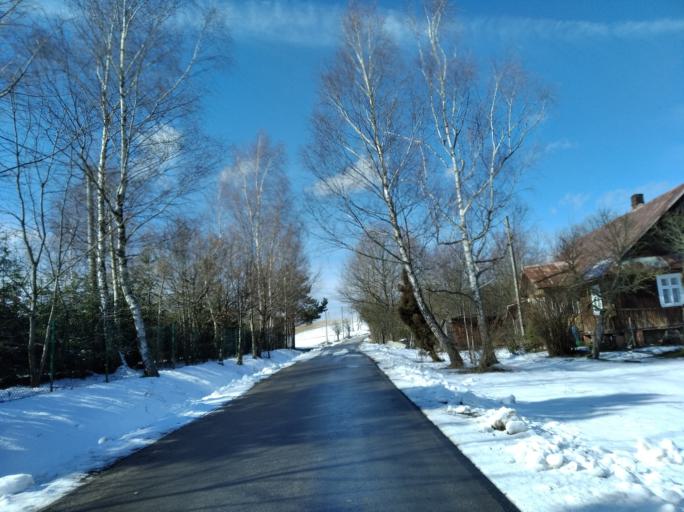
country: PL
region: Subcarpathian Voivodeship
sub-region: Powiat brzozowski
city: Jablonica Polska
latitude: 49.7318
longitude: 21.8601
